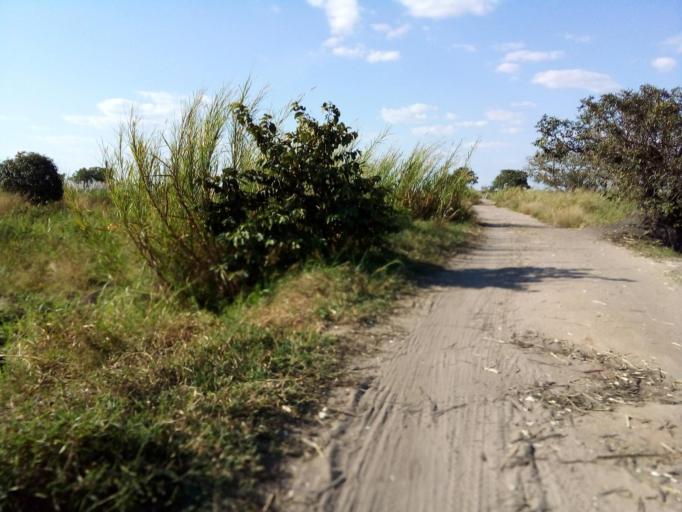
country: MZ
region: Zambezia
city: Quelimane
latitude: -17.5861
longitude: 36.8407
